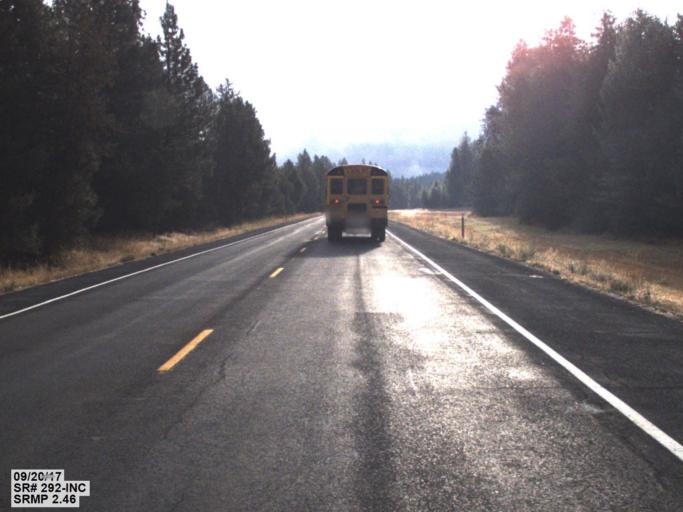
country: US
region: Washington
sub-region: Stevens County
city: Chewelah
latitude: 48.0658
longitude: -117.6917
